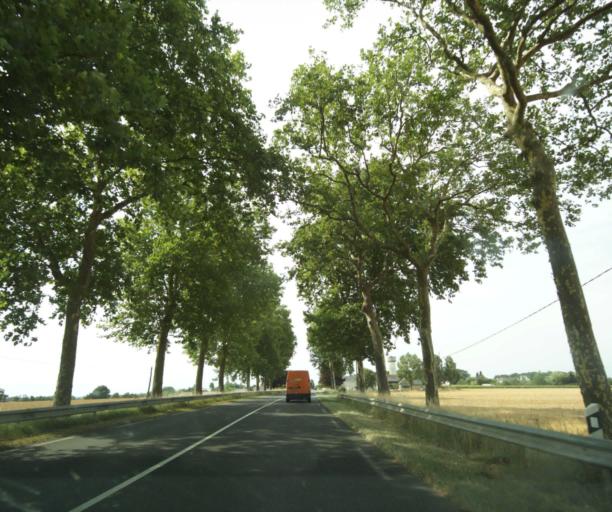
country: FR
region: Centre
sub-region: Departement d'Indre-et-Loire
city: Neuille-Pont-Pierre
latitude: 47.5401
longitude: 0.5566
